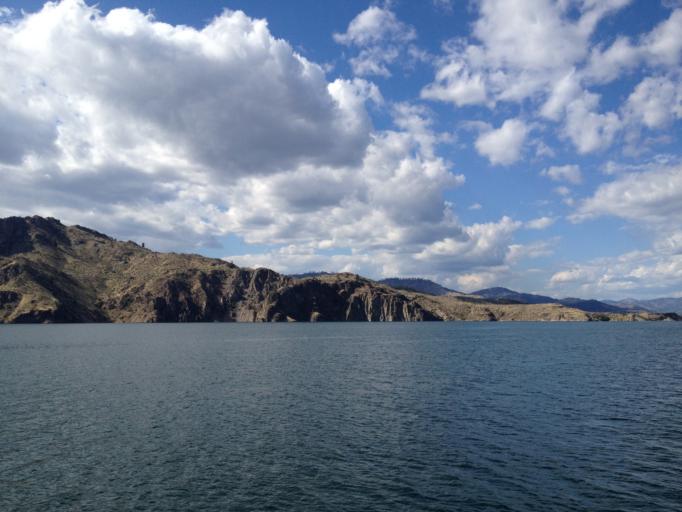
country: US
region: Washington
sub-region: Okanogan County
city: Coulee Dam
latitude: 47.9324
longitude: -118.6917
